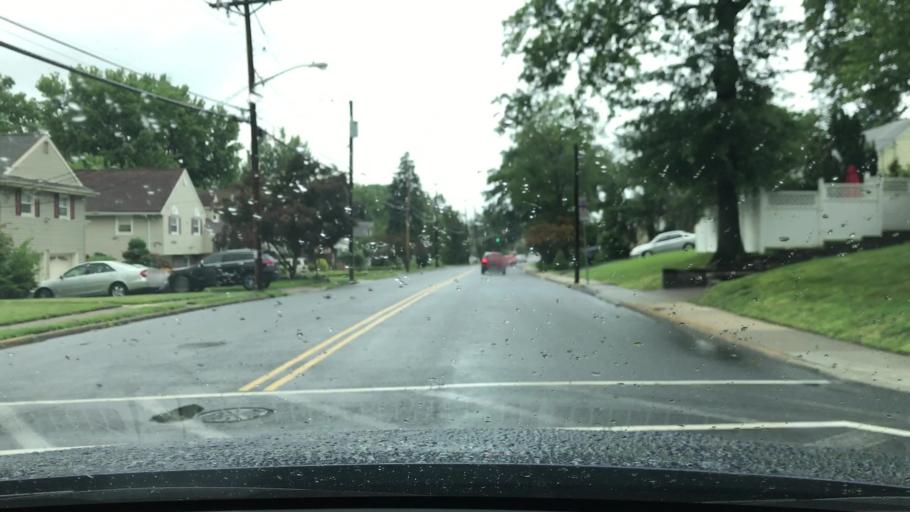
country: US
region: New Jersey
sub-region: Bergen County
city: New Milford
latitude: 40.9293
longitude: -74.0173
